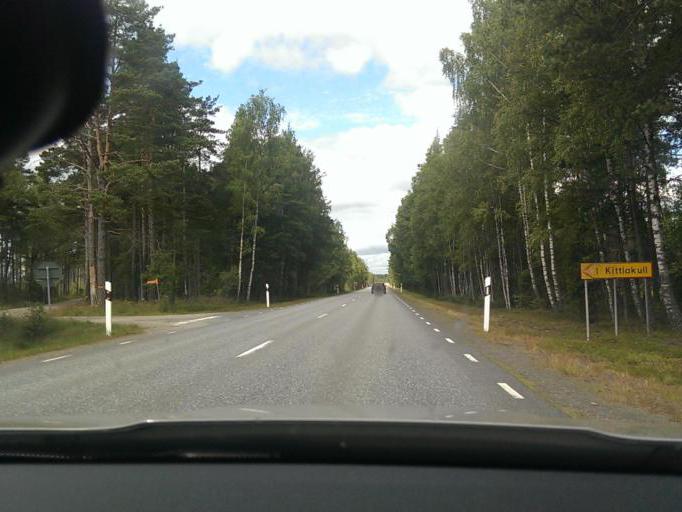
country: SE
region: Joenkoeping
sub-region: Gnosjo Kommun
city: Hillerstorp
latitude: 57.2874
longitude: 13.9552
